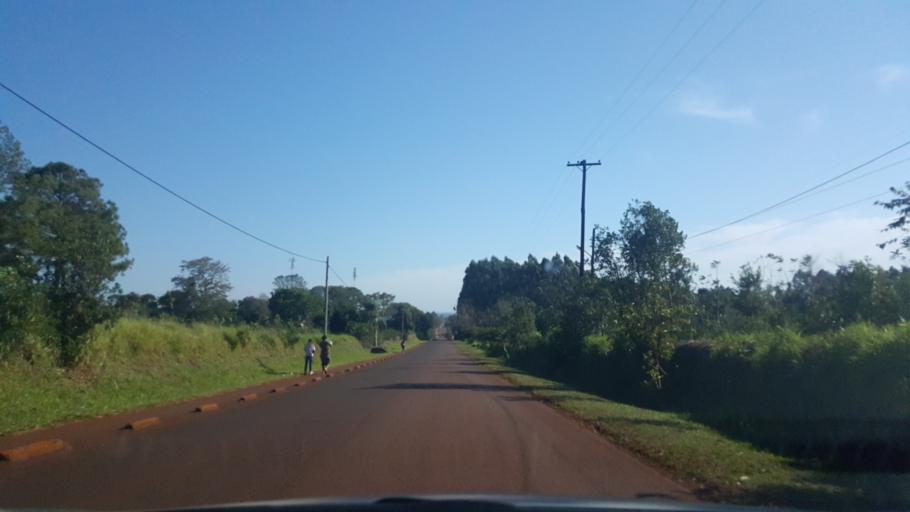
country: AR
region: Misiones
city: Santo Pipo
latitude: -27.1464
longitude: -55.4003
